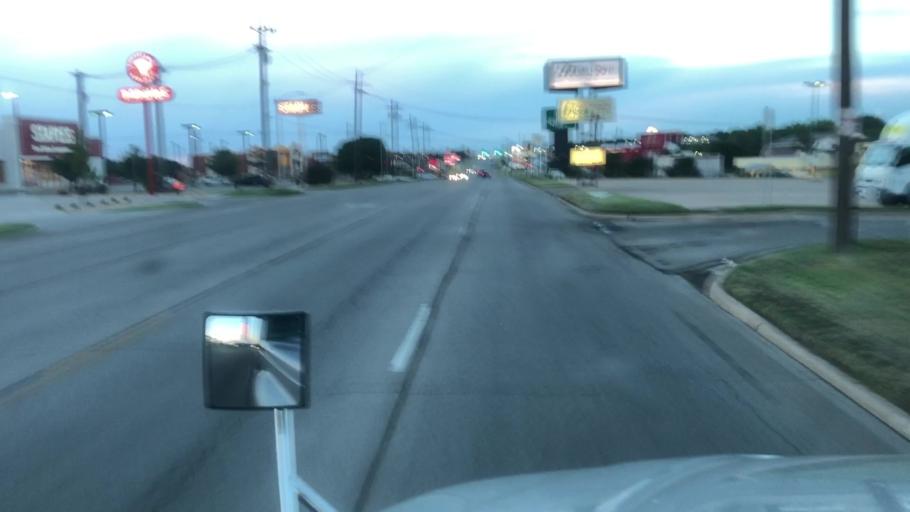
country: US
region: Oklahoma
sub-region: Kay County
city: Ponca City
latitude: 36.7295
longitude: -97.0672
